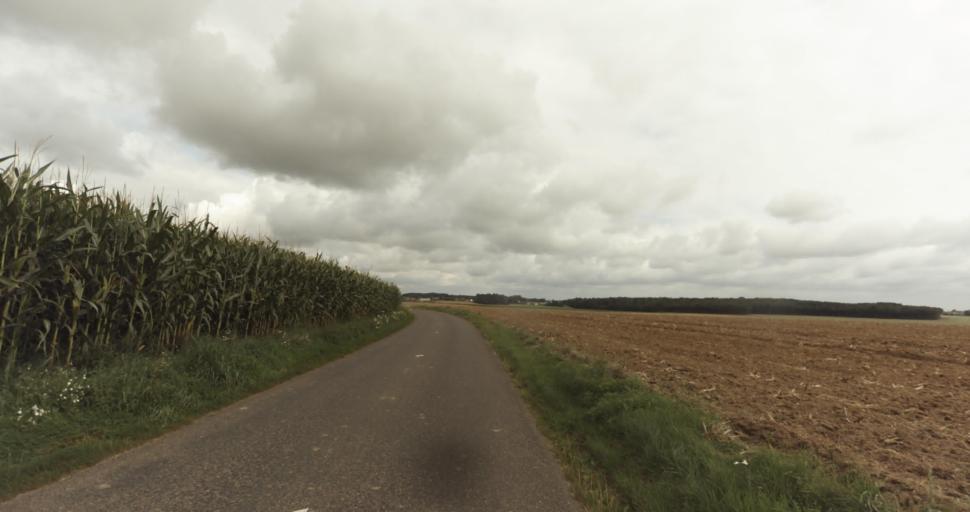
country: FR
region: Haute-Normandie
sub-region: Departement de l'Eure
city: Menilles
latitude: 48.9634
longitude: 1.2895
